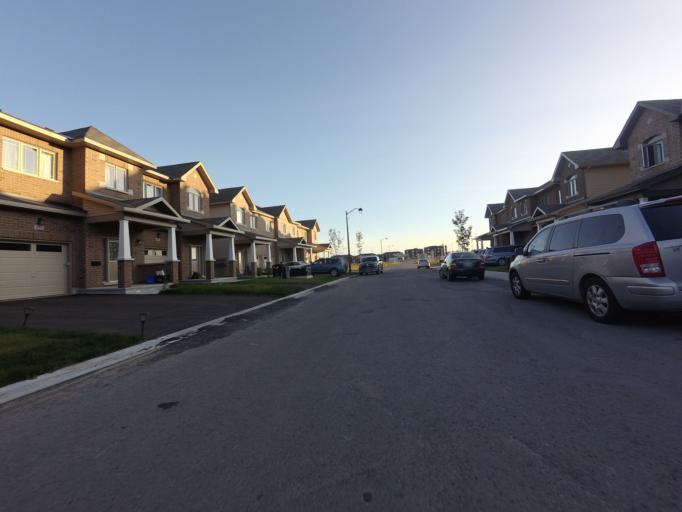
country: CA
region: Ontario
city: Bells Corners
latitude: 45.2868
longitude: -75.7448
